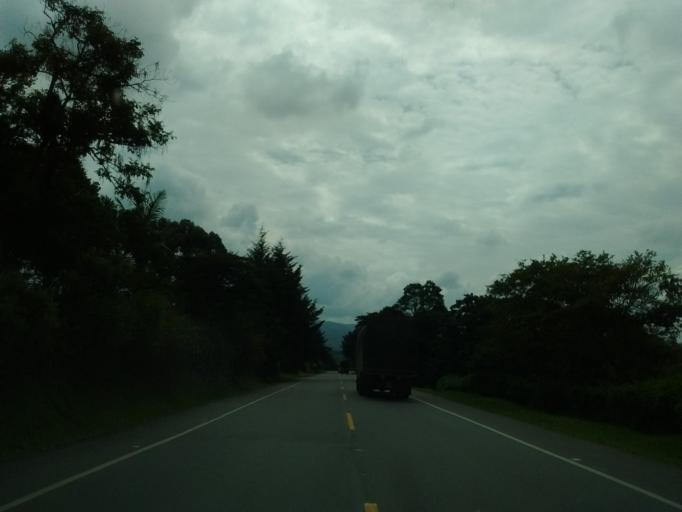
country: CO
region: Cauca
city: Morales
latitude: 2.7523
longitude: -76.5525
